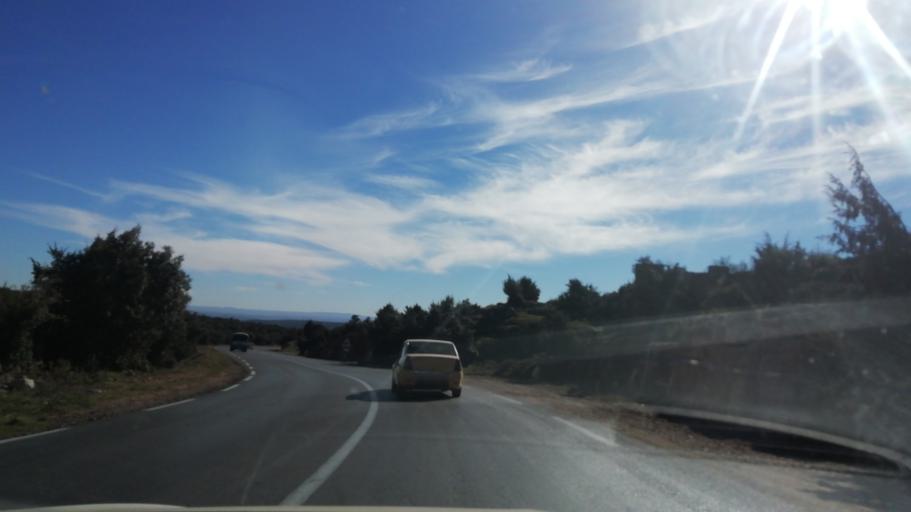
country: DZ
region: Tlemcen
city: Mansoura
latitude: 34.7518
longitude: -1.3447
